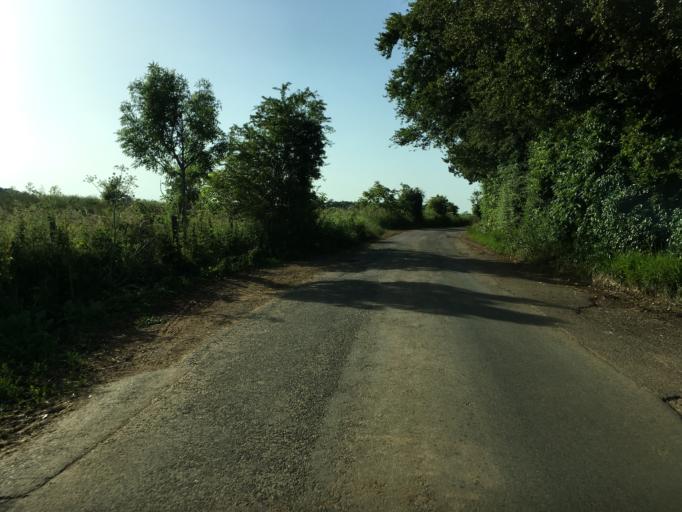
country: GB
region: England
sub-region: Oxfordshire
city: Burford
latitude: 51.7777
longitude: -1.7033
